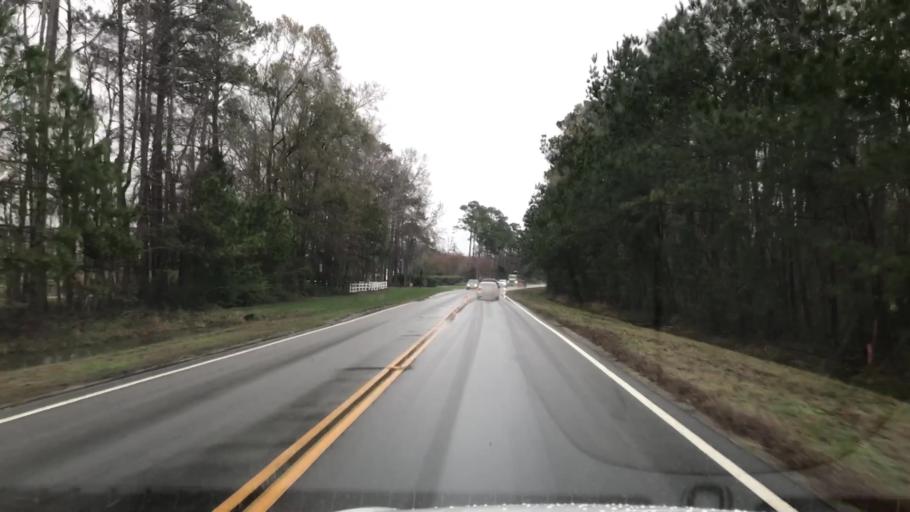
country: US
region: South Carolina
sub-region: Horry County
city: Myrtle Beach
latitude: 33.7303
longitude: -78.9085
